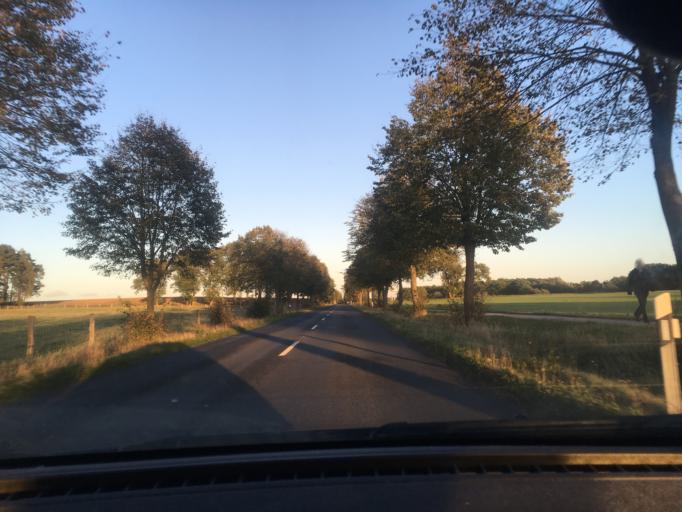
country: DE
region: Lower Saxony
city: Wendisch Evern
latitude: 53.2206
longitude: 10.4708
